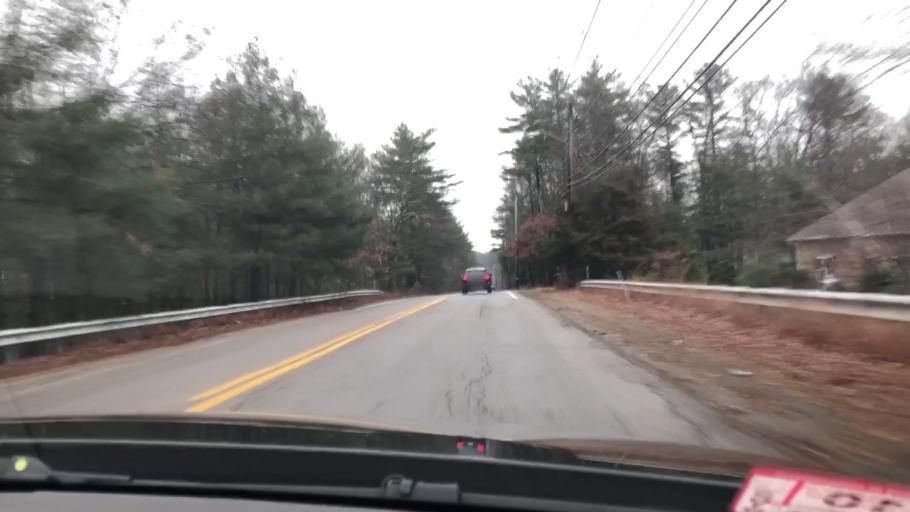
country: US
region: Massachusetts
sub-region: Norfolk County
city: Norfolk
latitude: 42.1066
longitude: -71.2865
